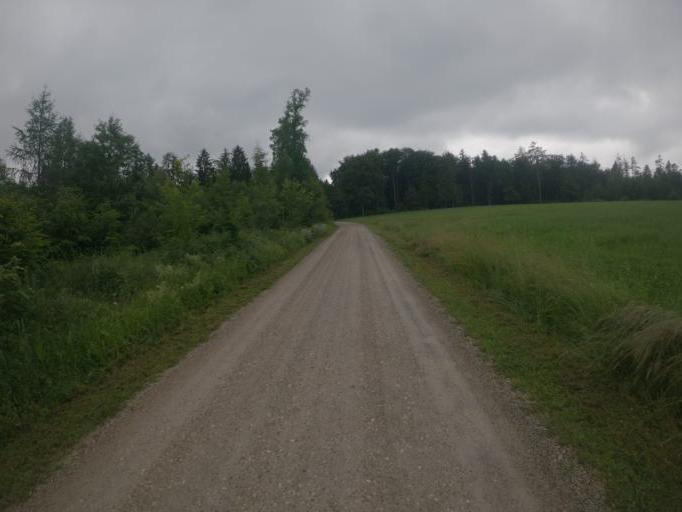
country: DE
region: Baden-Wuerttemberg
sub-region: Regierungsbezirk Stuttgart
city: Schorndorf
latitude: 48.7709
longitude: 9.5401
